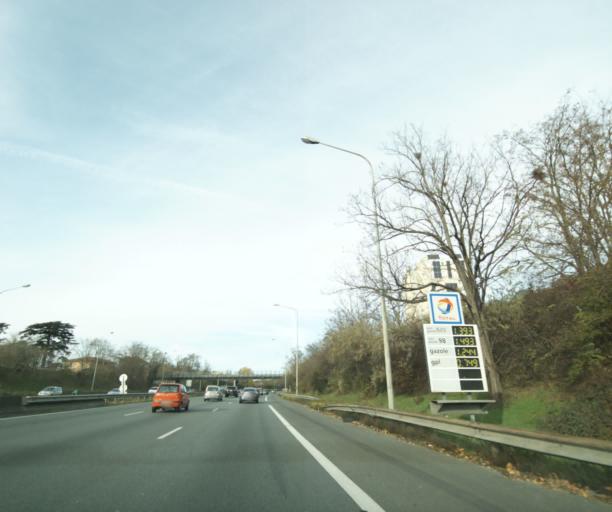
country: FR
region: Midi-Pyrenees
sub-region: Departement de la Haute-Garonne
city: Blagnac
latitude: 43.5949
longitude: 1.3976
